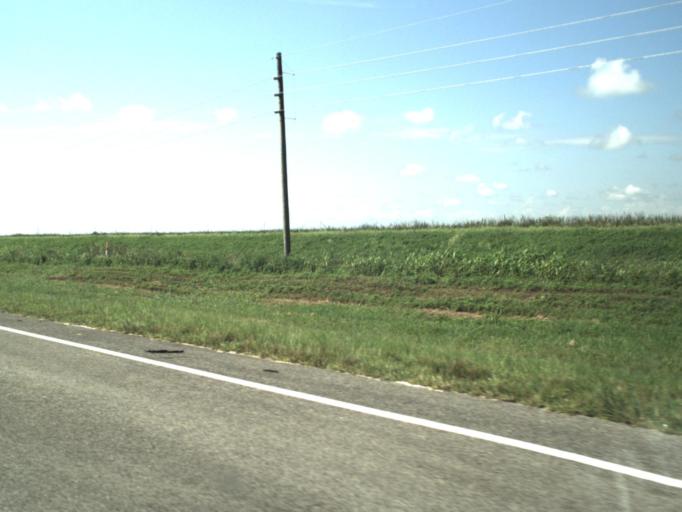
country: US
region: Florida
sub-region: Palm Beach County
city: Belle Glade Camp
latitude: 26.3754
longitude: -80.5693
